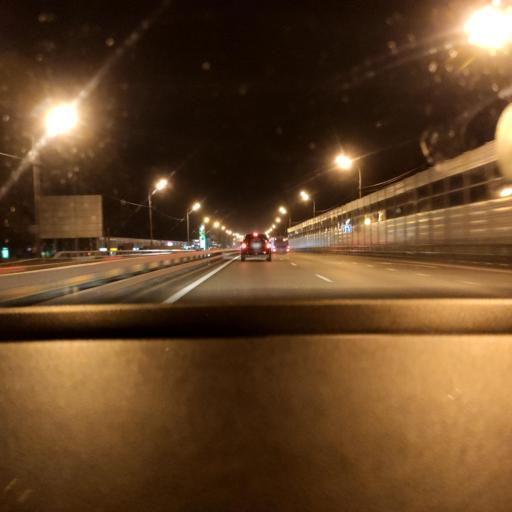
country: RU
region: Moskovskaya
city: Selyatino
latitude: 55.5122
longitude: 36.9889
